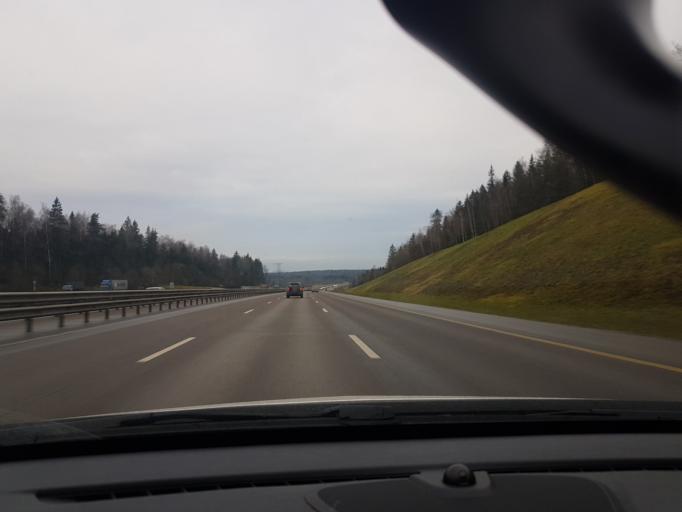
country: RU
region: Moskovskaya
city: Kostrovo
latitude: 55.8748
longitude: 36.6856
